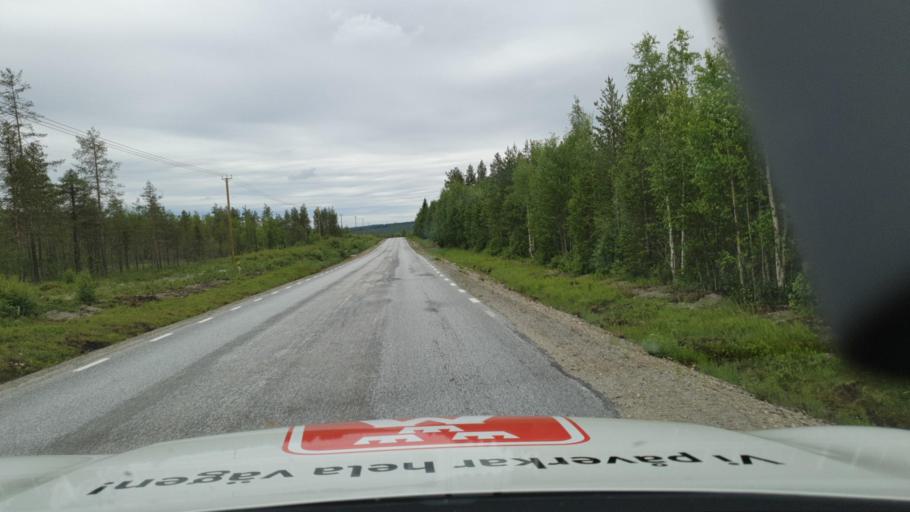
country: SE
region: Vaesterbotten
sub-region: Lycksele Kommun
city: Lycksele
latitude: 64.1112
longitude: 18.3634
